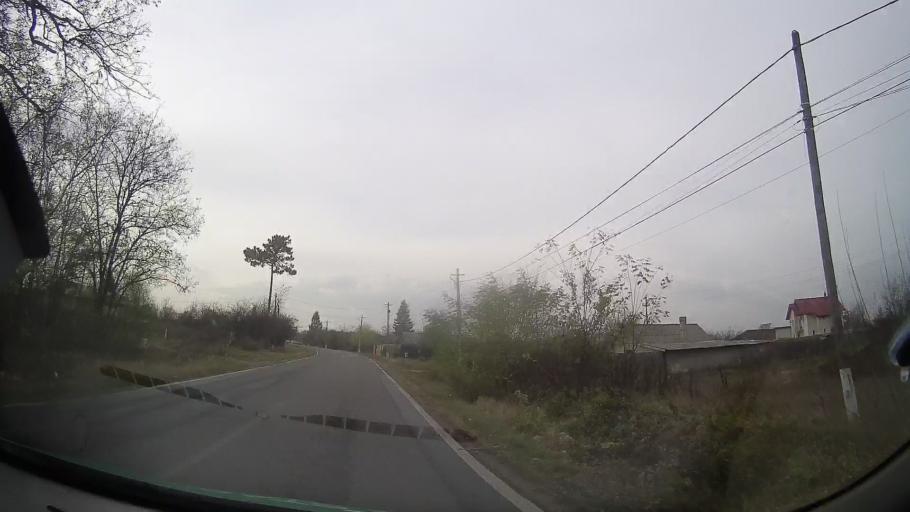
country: RO
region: Prahova
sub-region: Comuna Balta Doamnei
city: Balta Doamnei
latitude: 44.7436
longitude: 26.1317
